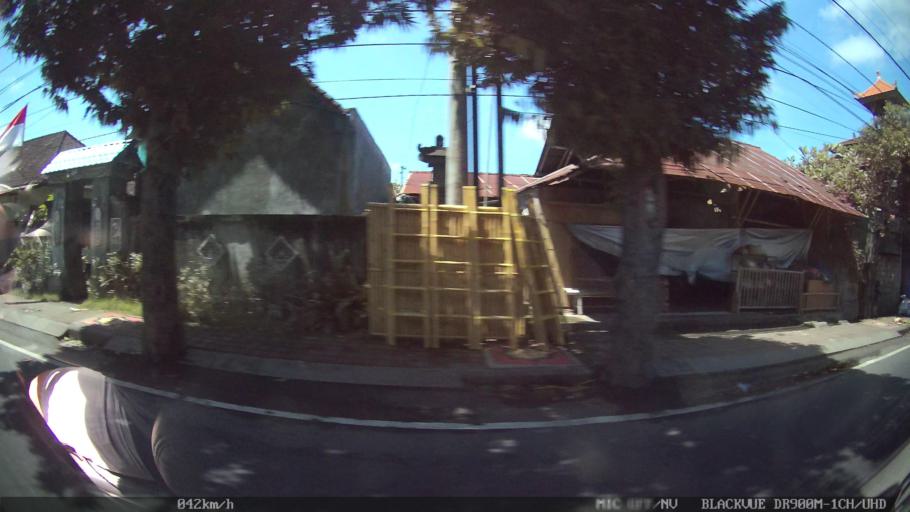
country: ID
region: Bali
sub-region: Kabupaten Gianyar
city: Ubud
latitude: -8.5638
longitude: 115.3088
